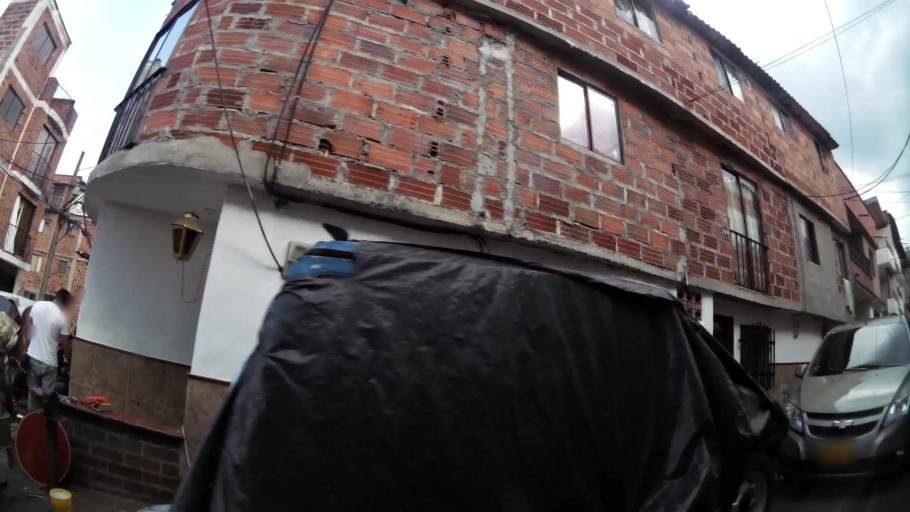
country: CO
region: Antioquia
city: Envigado
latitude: 6.1575
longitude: -75.5854
